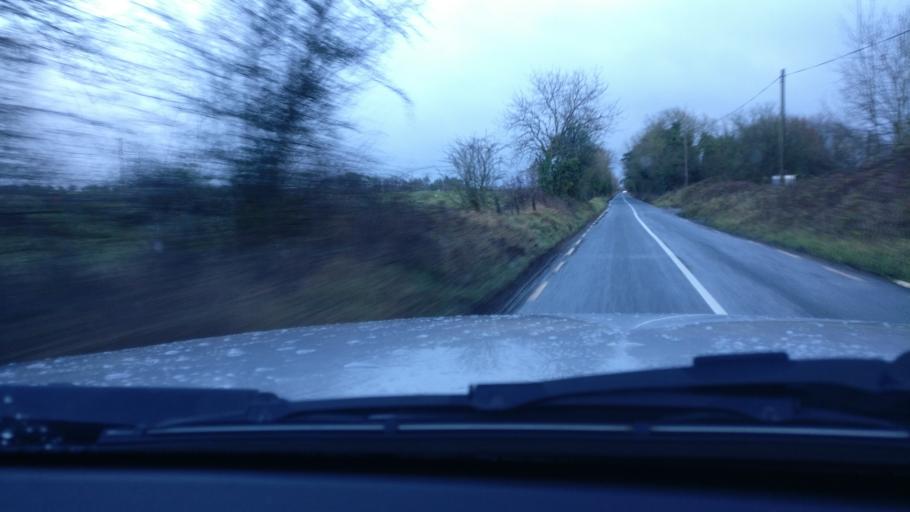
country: IE
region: Connaught
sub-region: County Galway
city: Loughrea
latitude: 53.2240
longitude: -8.3903
